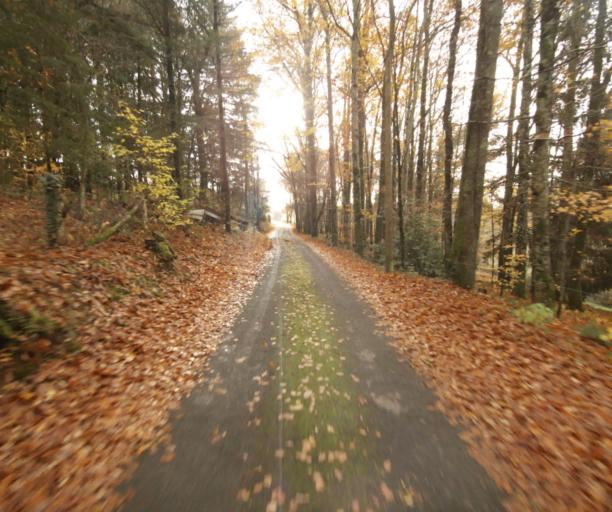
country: FR
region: Limousin
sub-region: Departement de la Correze
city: Cornil
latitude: 45.2010
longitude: 1.7111
